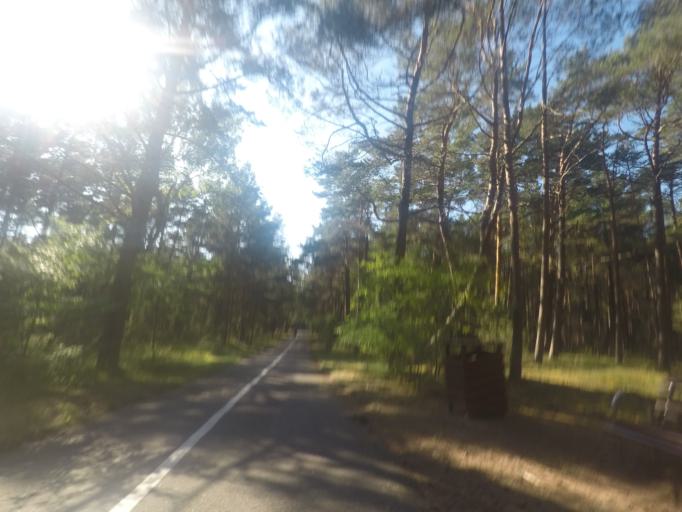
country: LT
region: Klaipedos apskritis
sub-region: Klaipeda
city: Klaipeda
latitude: 55.5479
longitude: 21.1057
